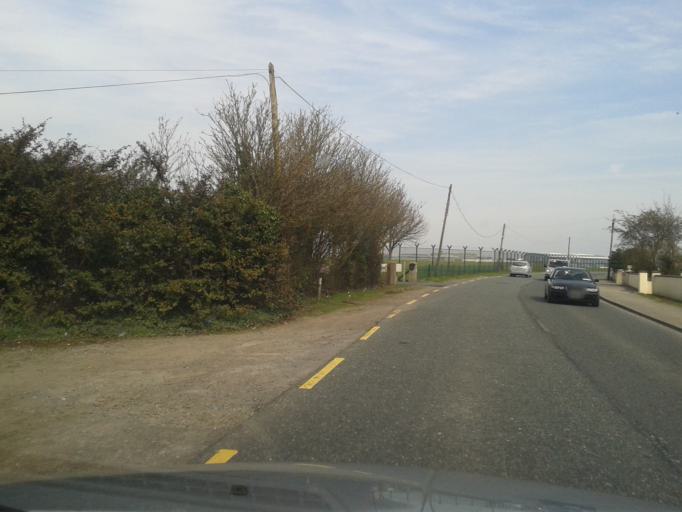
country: IE
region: Leinster
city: Ballymun
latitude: 53.4182
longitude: -6.2632
